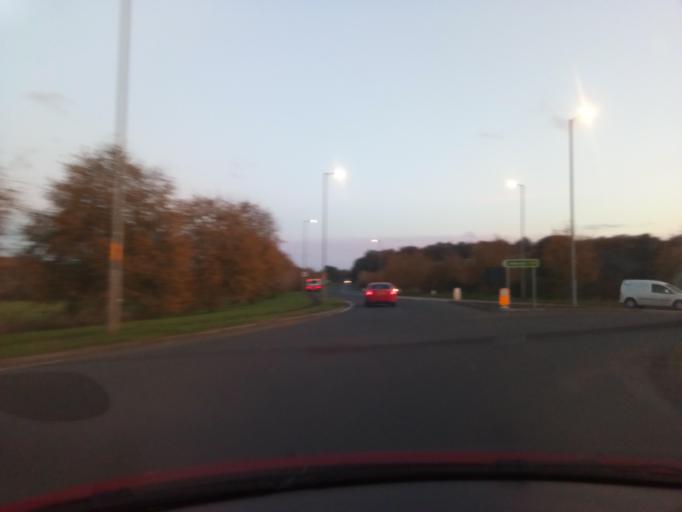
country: GB
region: Scotland
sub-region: The Scottish Borders
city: Lauder
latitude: 55.7710
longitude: -2.7874
